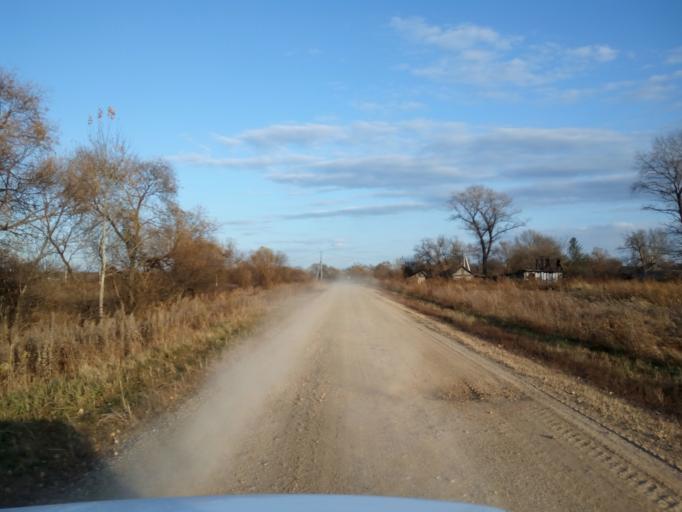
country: RU
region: Primorskiy
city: Lazo
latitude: 45.8251
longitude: 133.6090
